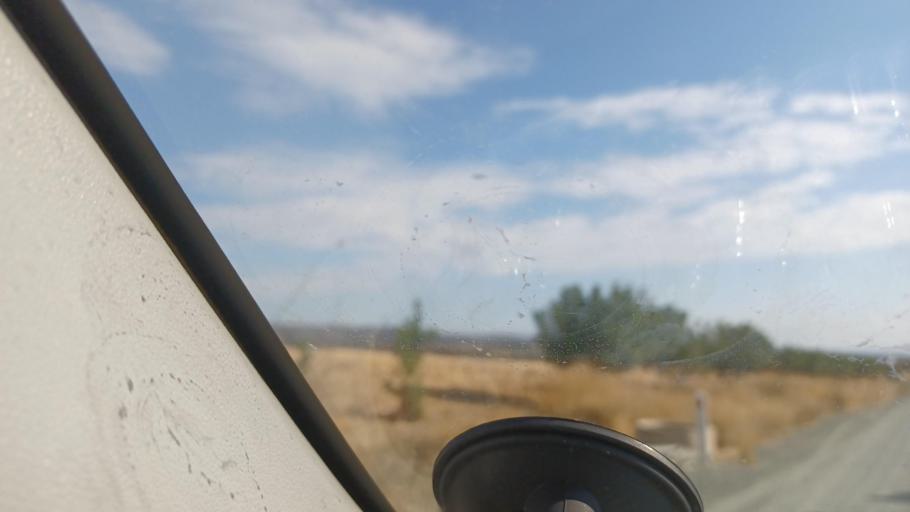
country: CY
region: Pafos
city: Mesogi
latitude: 34.7342
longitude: 32.5485
